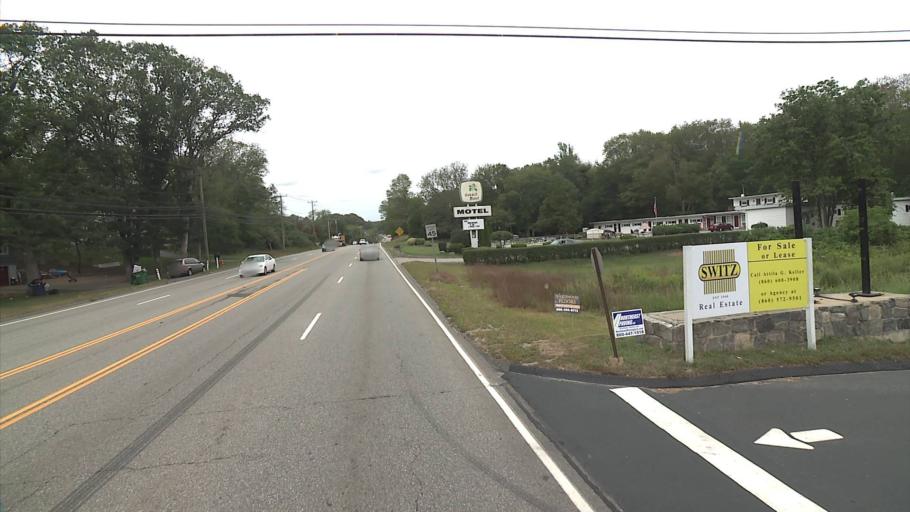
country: US
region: Connecticut
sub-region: New London County
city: Central Waterford
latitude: 41.3881
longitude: -72.1599
